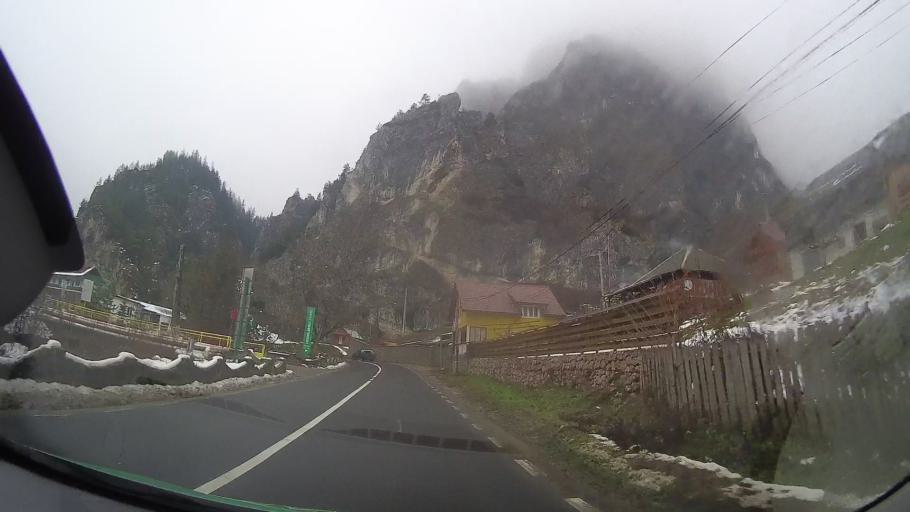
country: RO
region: Neamt
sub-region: Comuna Bicaz Chei
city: Bicaz Chei
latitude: 46.8243
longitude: 25.8534
